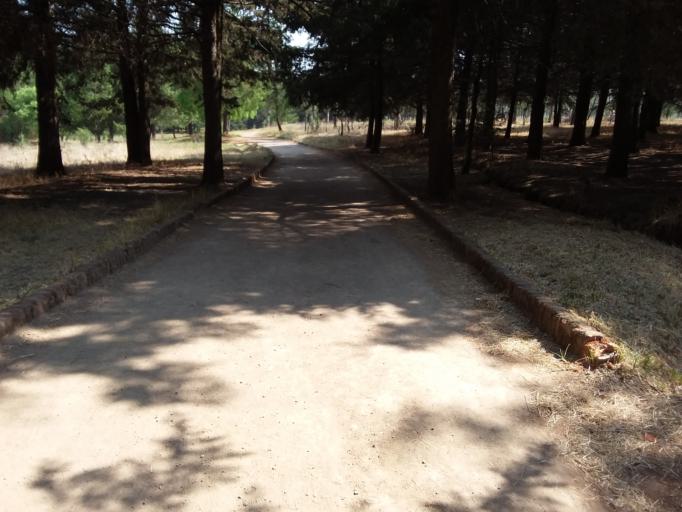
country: MX
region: Mexico
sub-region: Toluca
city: San Antonio Buenavista
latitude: 19.2706
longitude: -99.7003
